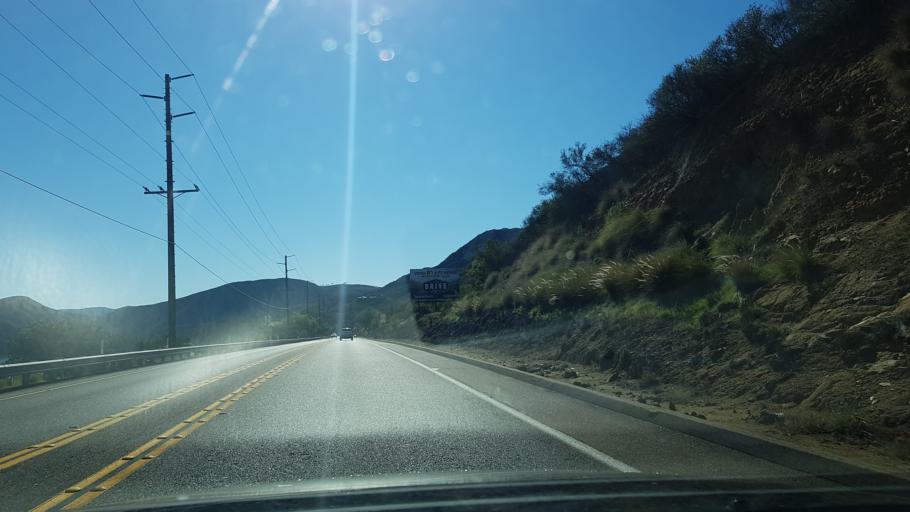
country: US
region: California
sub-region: San Diego County
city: Escondido
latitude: 33.0714
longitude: -117.1218
